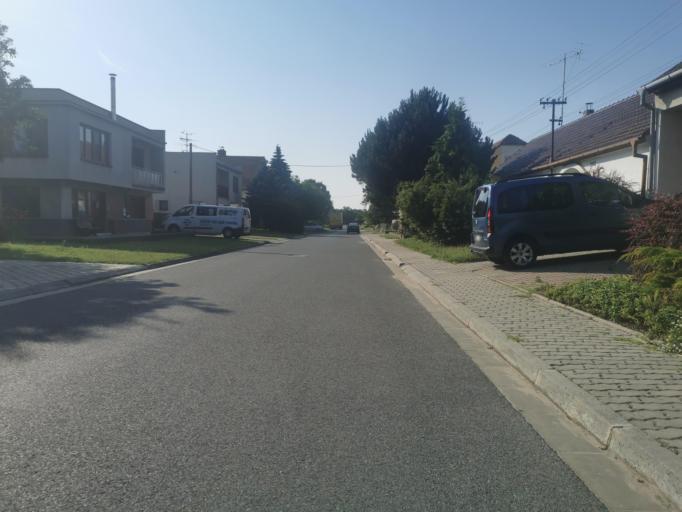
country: CZ
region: South Moravian
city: Vacenovice
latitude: 48.9406
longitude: 17.1796
